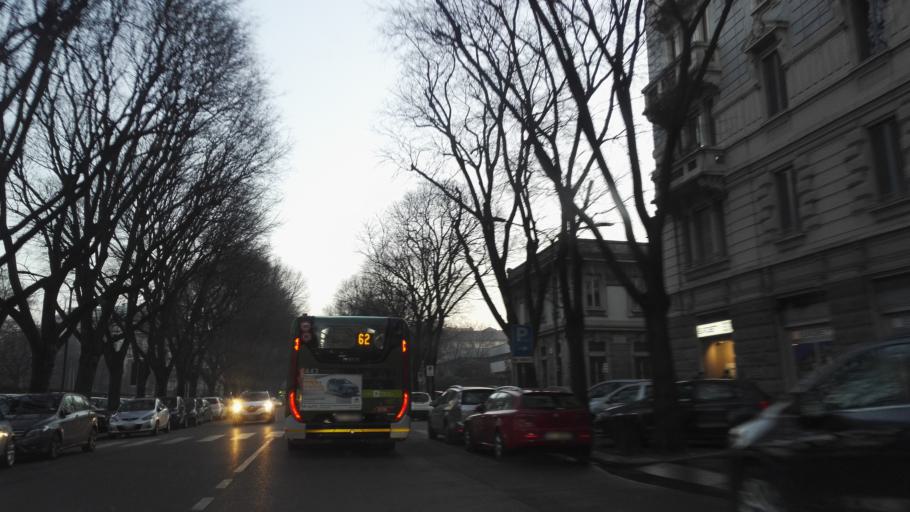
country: IT
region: Lombardy
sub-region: Citta metropolitana di Milano
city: Milano
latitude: 45.4612
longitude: 9.2146
